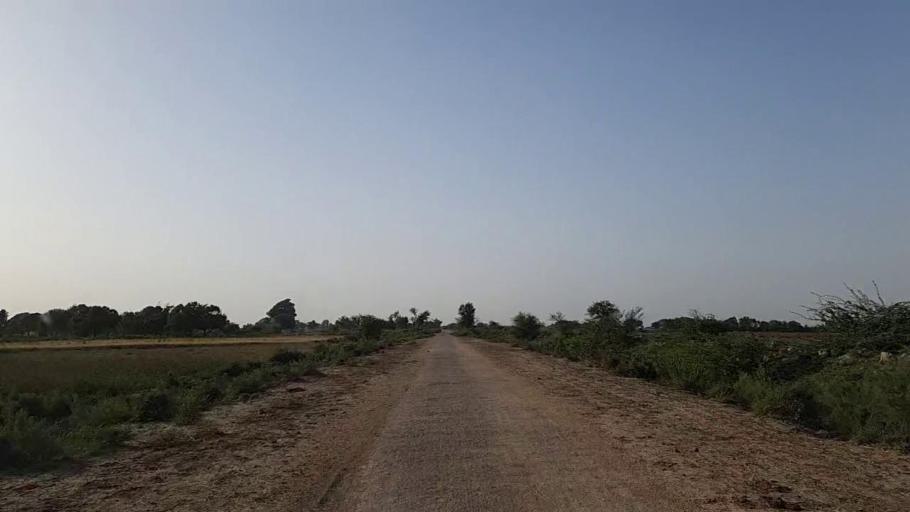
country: PK
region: Sindh
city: Jati
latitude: 24.3245
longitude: 68.1648
